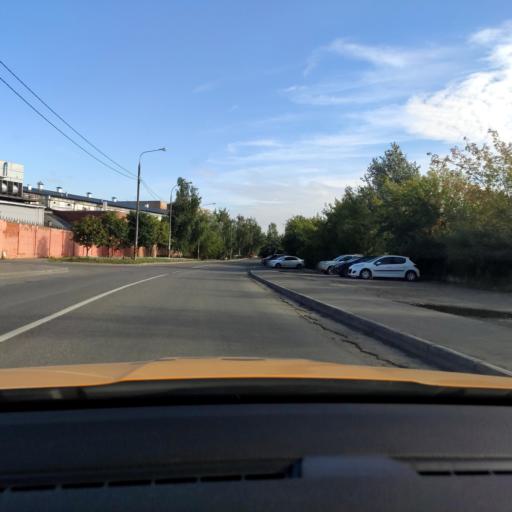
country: RU
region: Moscow
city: Tsaritsyno
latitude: 55.6309
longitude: 37.6306
